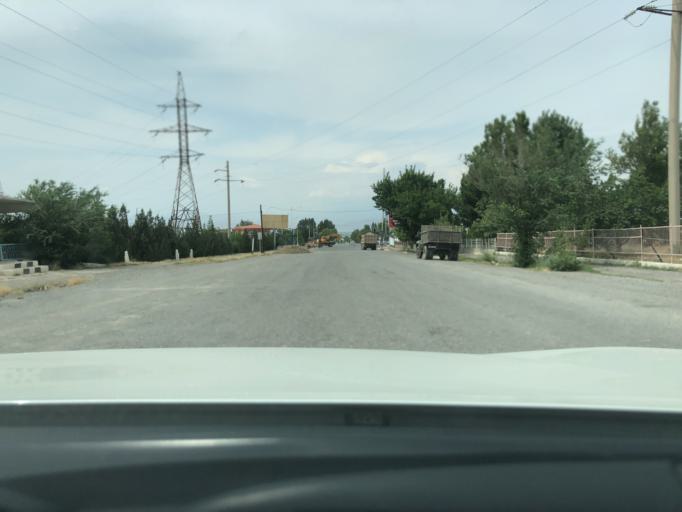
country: TJ
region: Viloyati Sughd
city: Konibodom
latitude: 40.2756
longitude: 70.4450
